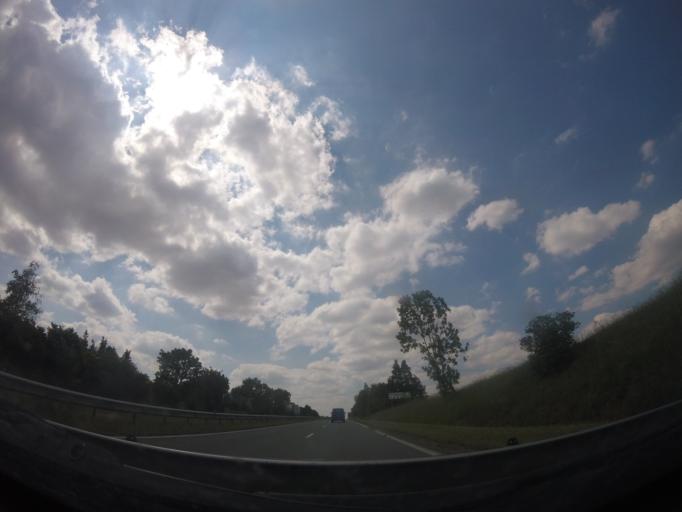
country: FR
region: Poitou-Charentes
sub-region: Departement de la Charente-Maritime
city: Saint-Porchaire
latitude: 45.8125
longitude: -0.7737
